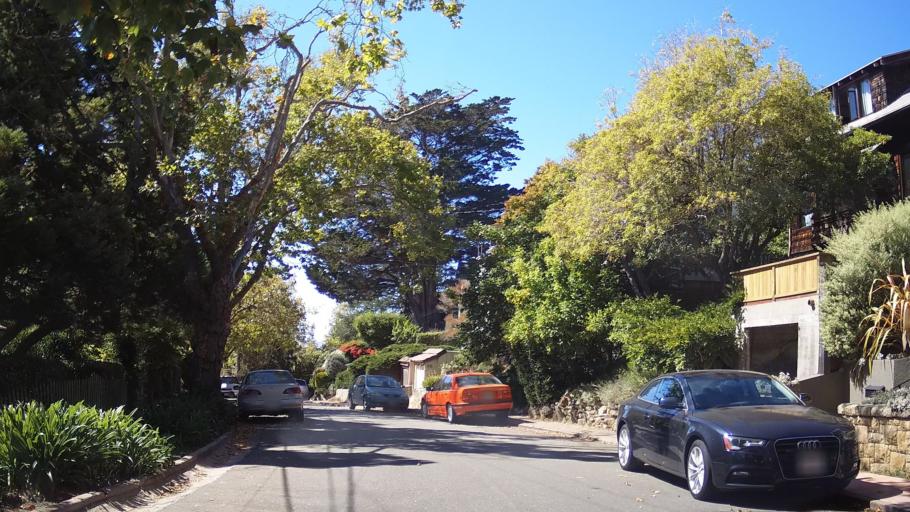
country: US
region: California
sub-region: Alameda County
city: Berkeley
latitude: 37.8911
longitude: -122.2690
